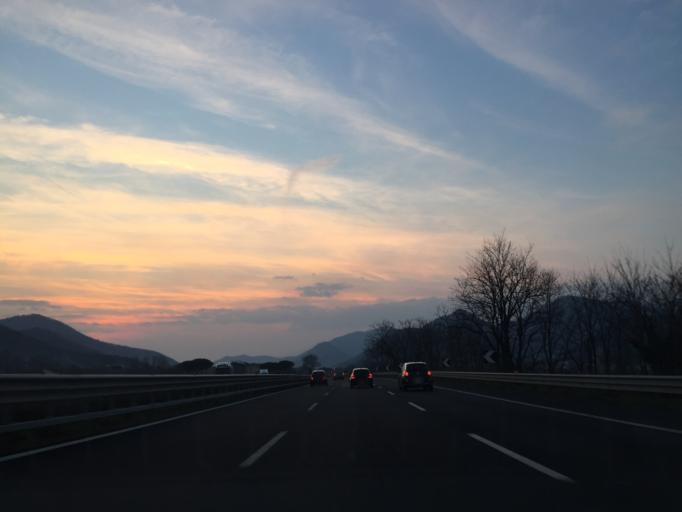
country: IT
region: Campania
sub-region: Provincia di Salerno
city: Faraldo-Nocelleto
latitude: 40.7740
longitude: 14.7646
